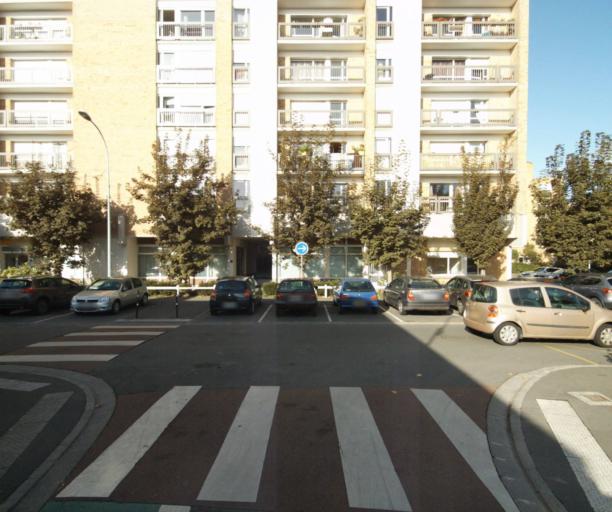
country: FR
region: Nord-Pas-de-Calais
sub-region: Departement du Nord
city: La Madeleine
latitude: 50.6520
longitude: 3.0695
